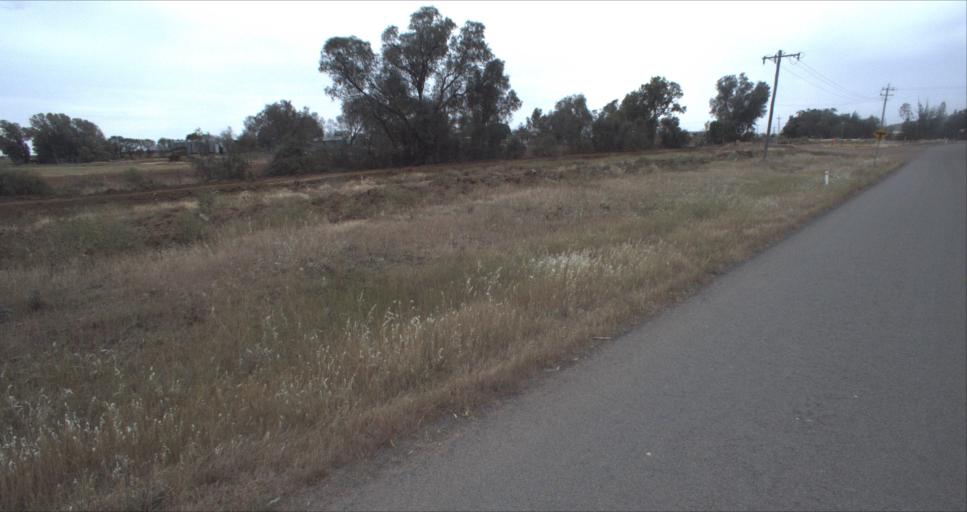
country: AU
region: New South Wales
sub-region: Leeton
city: Leeton
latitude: -34.4439
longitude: 146.3752
